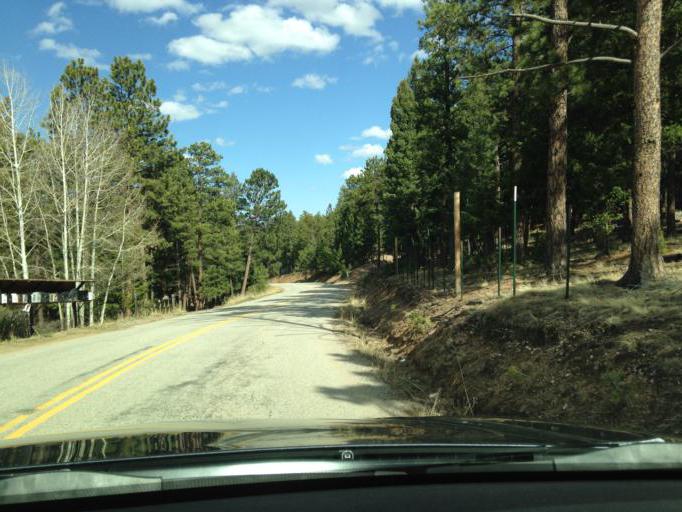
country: US
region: Colorado
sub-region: Jefferson County
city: Evergreen
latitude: 39.4306
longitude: -105.4171
